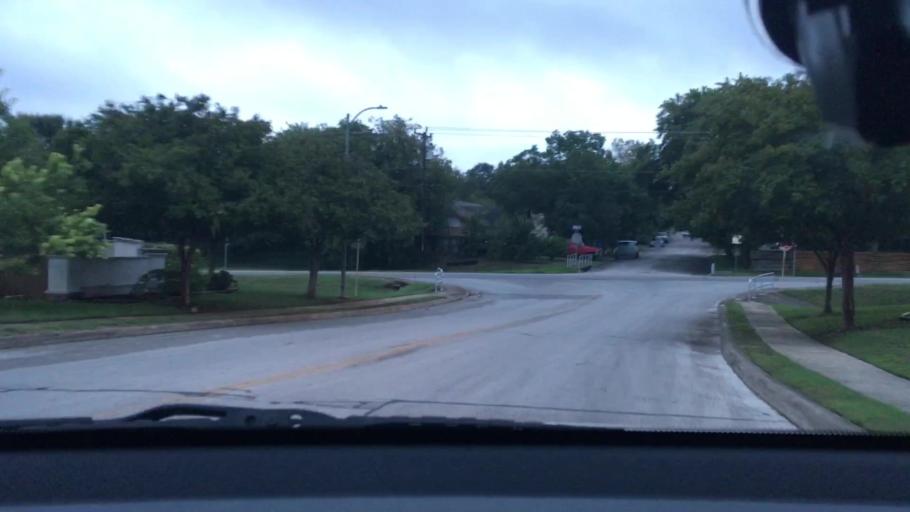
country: US
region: Texas
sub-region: Bexar County
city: Live Oak
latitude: 29.5938
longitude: -98.3656
